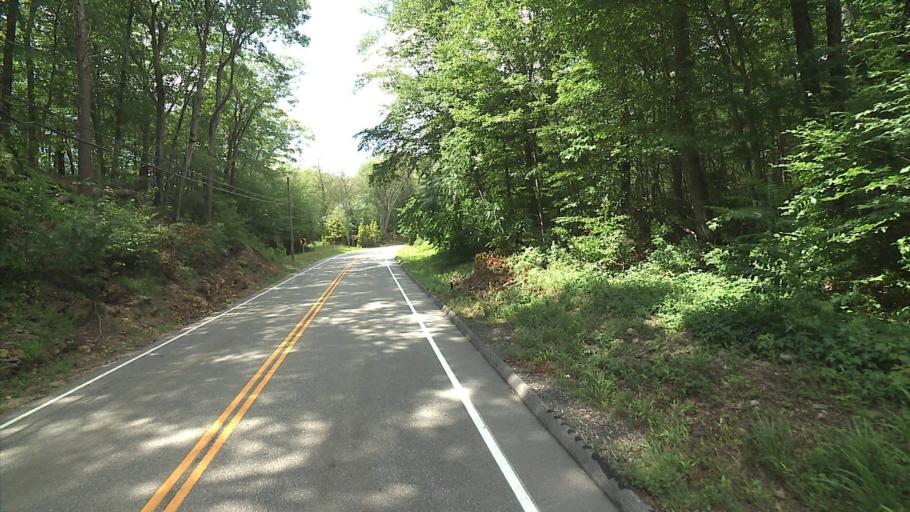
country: US
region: Connecticut
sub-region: Middlesex County
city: Clinton
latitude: 41.3244
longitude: -72.5477
